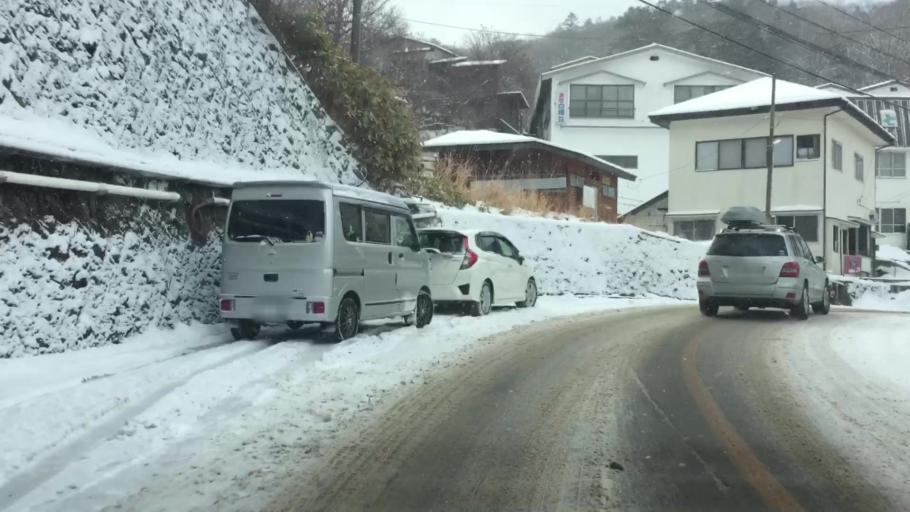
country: JP
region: Tochigi
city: Yaita
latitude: 36.9552
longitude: 139.7795
